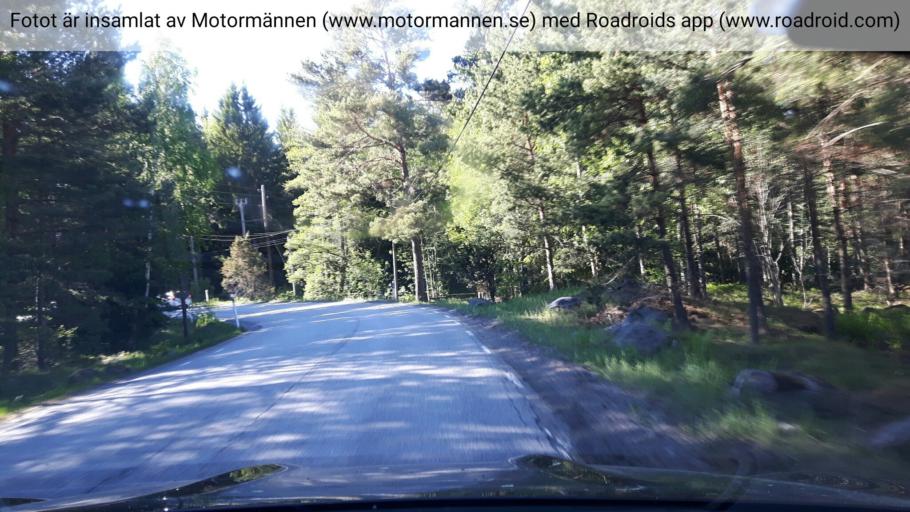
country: SE
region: Stockholm
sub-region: Norrtalje Kommun
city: Norrtalje
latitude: 59.6821
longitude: 18.8357
